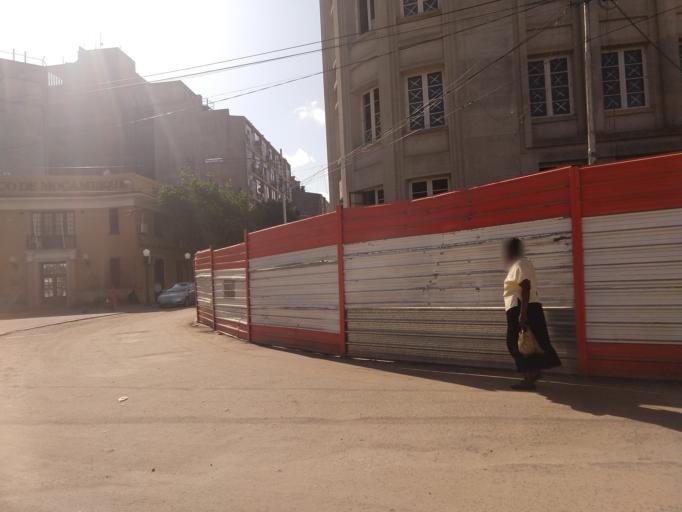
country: MZ
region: Sofala
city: Beira
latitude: -19.8317
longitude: 34.8348
